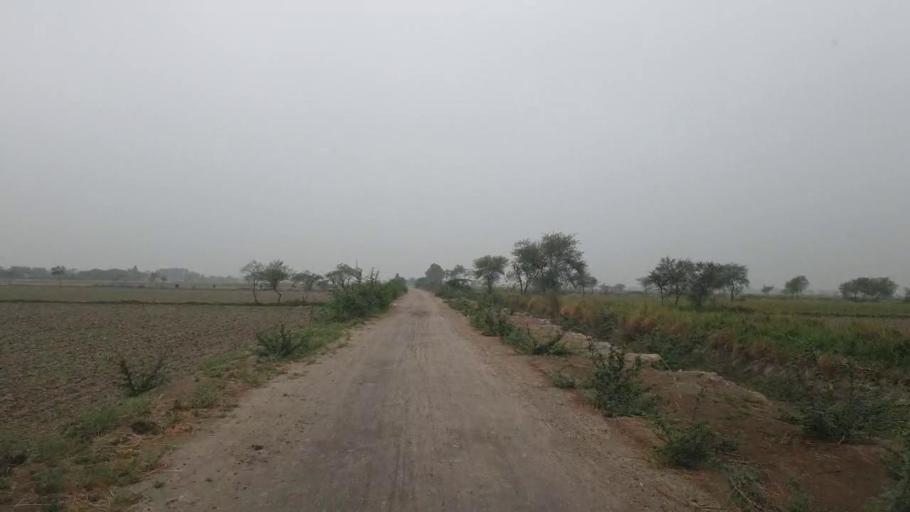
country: PK
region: Sindh
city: Badin
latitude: 24.5706
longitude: 68.6552
